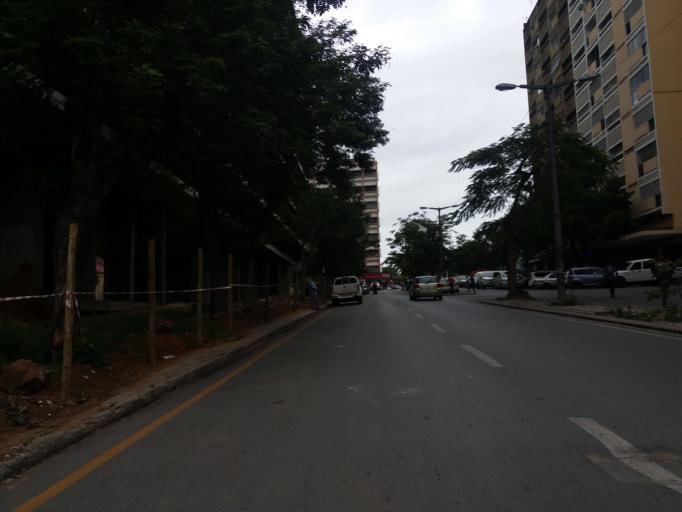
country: MZ
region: Maputo City
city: Maputo
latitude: -25.9677
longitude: 32.5747
